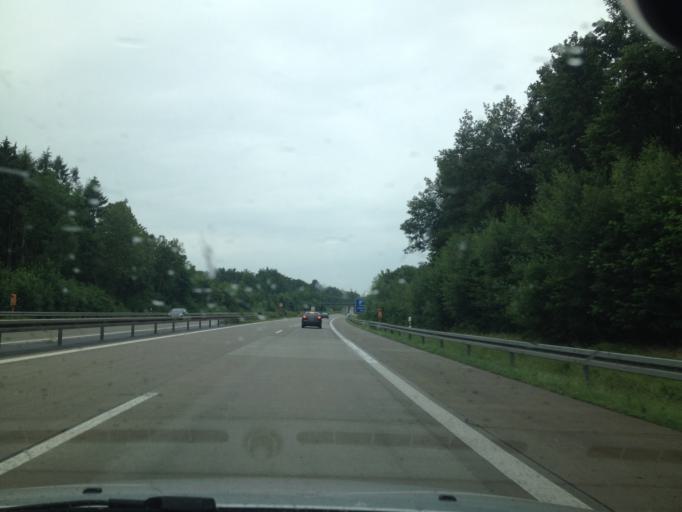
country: DE
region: Bavaria
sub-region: Regierungsbezirk Mittelfranken
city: Ohrenbach
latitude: 49.4979
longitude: 10.1986
